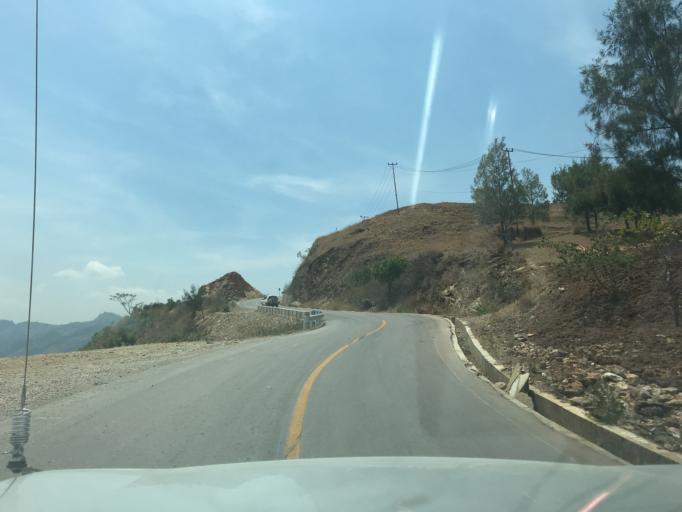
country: TL
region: Aileu
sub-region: Aileu Villa
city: Aileu
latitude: -8.8060
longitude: 125.5953
